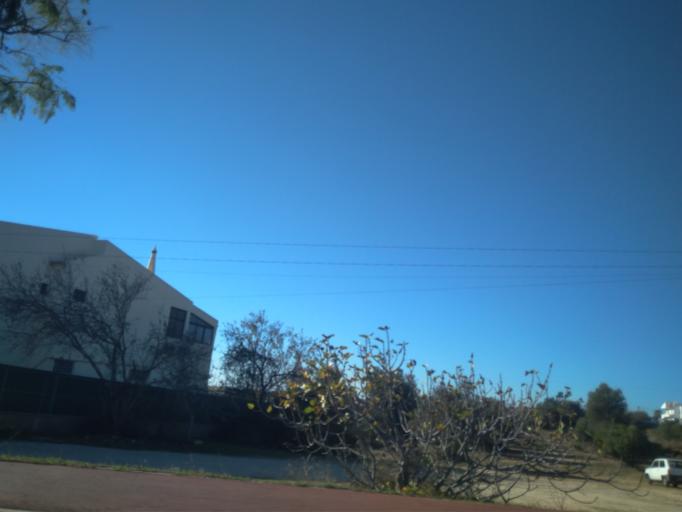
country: PT
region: Faro
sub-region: Albufeira
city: Ferreiras
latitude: 37.1145
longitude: -8.2299
